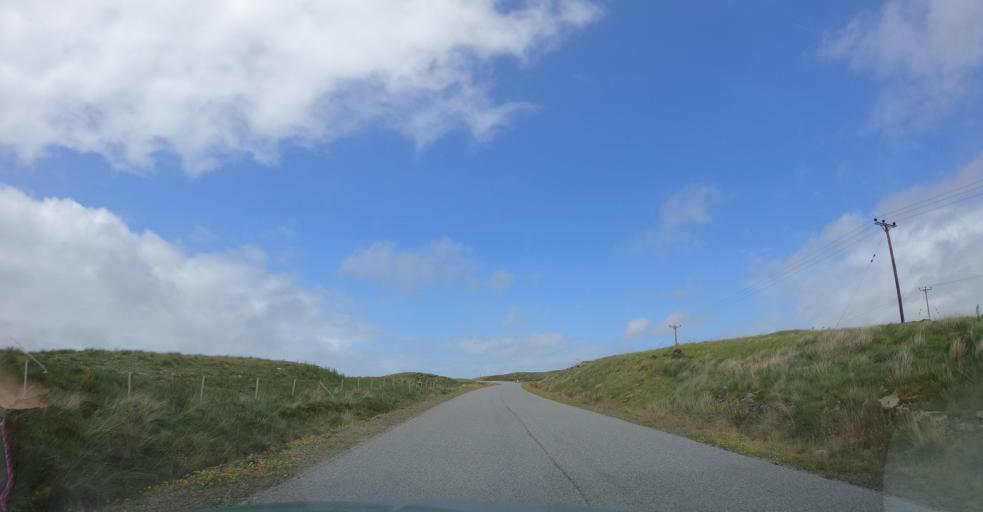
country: GB
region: Scotland
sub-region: Eilean Siar
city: Isle of South Uist
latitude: 57.2287
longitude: -7.3972
